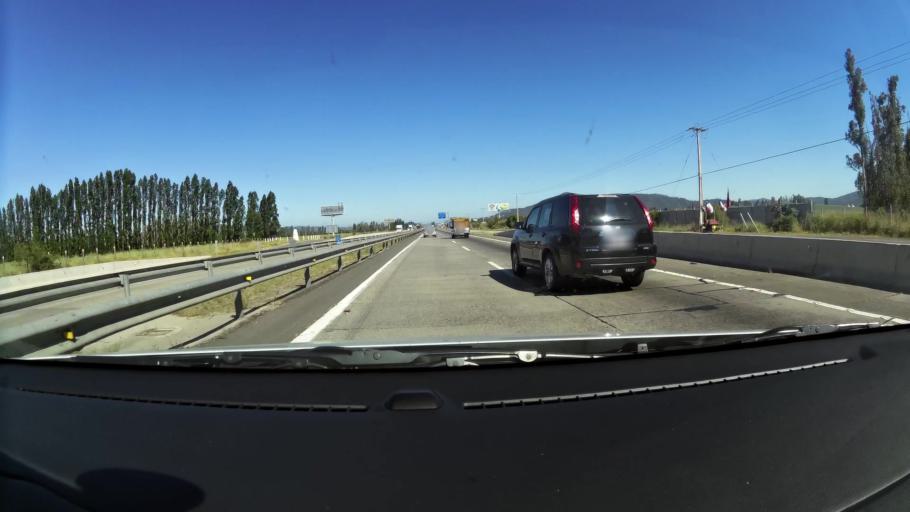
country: CL
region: Valparaiso
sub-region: Provincia de Marga Marga
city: Villa Alemana
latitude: -33.3530
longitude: -71.3385
